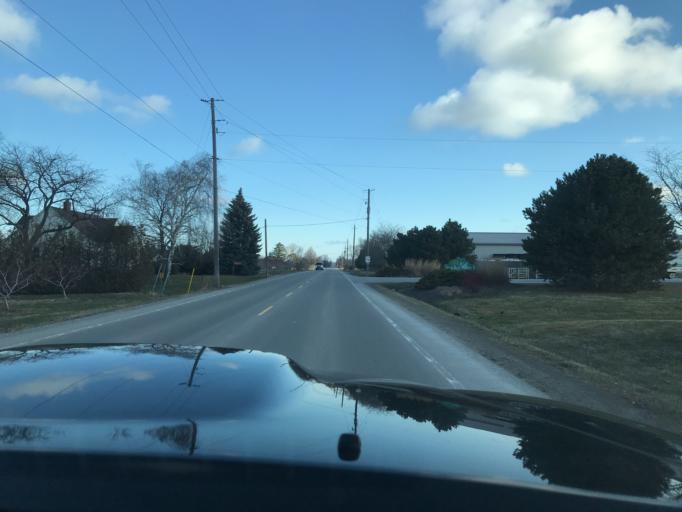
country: CA
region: Ontario
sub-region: Regional Municipality of Niagara
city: St. Catharines
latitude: 43.1590
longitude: -79.3079
